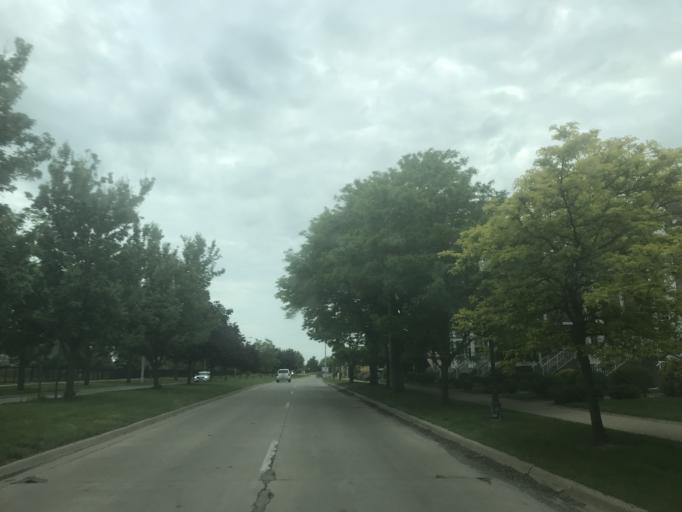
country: US
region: Michigan
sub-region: Wayne County
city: Wyandotte
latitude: 42.1946
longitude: -83.1534
